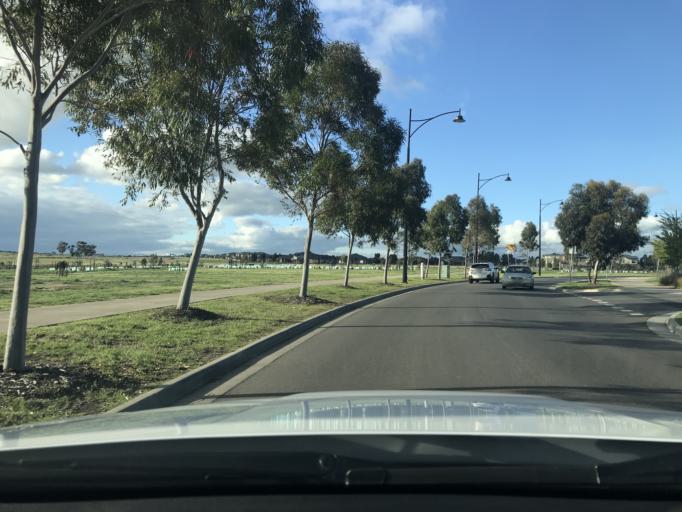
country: AU
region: Victoria
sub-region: Hume
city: Roxburgh Park
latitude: -37.5837
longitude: 144.9020
